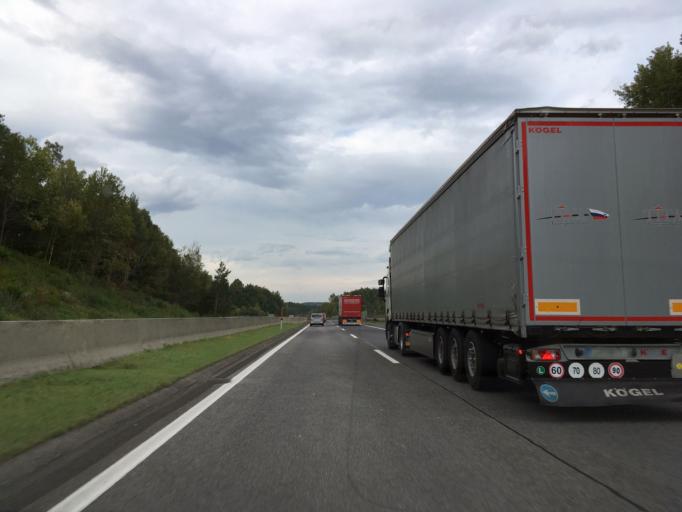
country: AT
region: Lower Austria
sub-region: Politischer Bezirk Neunkirchen
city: Warth
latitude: 47.6614
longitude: 16.1260
